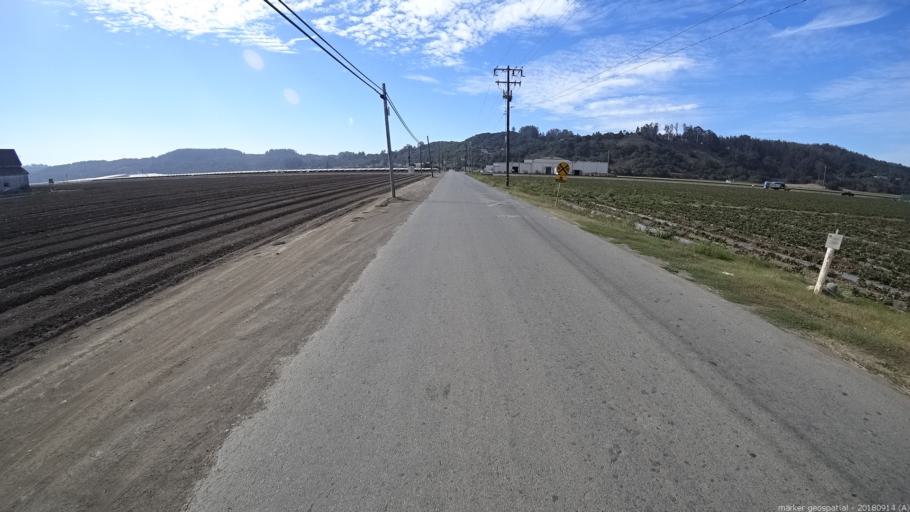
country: US
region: California
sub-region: San Benito County
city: Aromas
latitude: 36.8990
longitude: -121.6905
